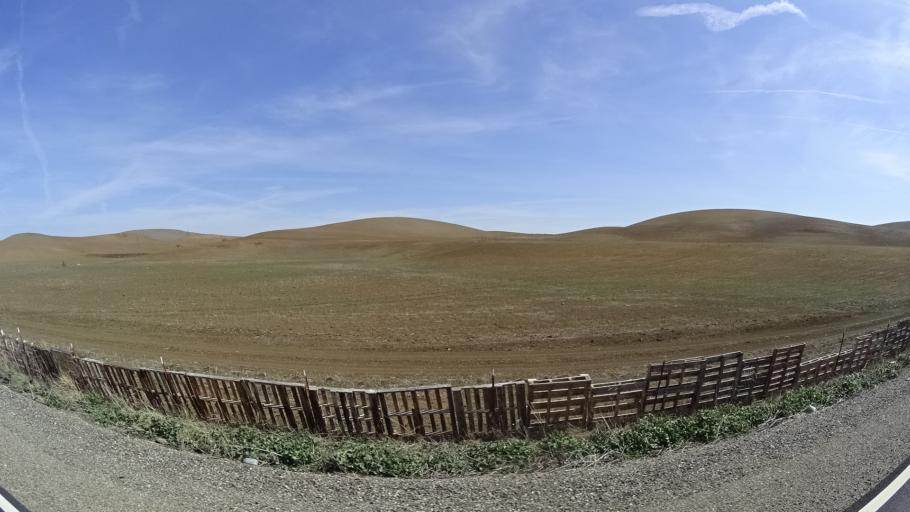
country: US
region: California
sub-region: Glenn County
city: Willows
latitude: 39.5467
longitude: -122.3507
